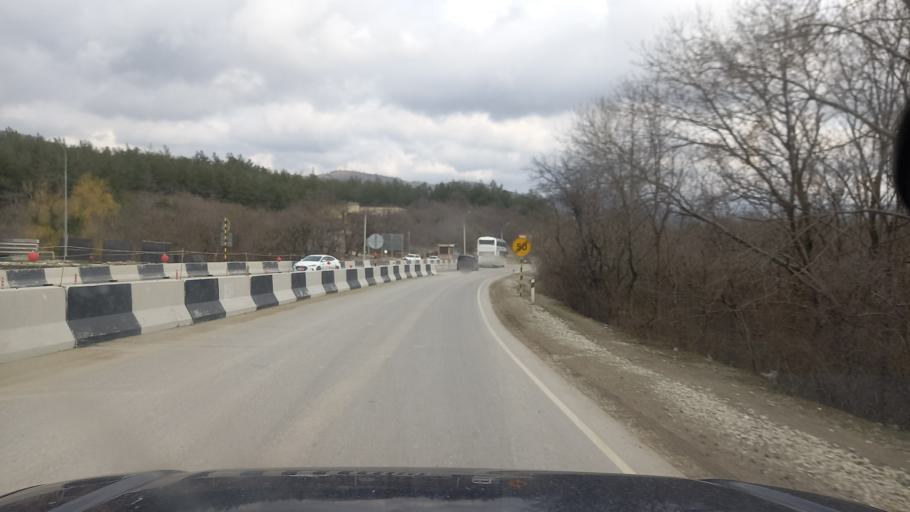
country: RU
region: Krasnodarskiy
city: Gelendzhik
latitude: 44.5551
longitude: 38.1247
